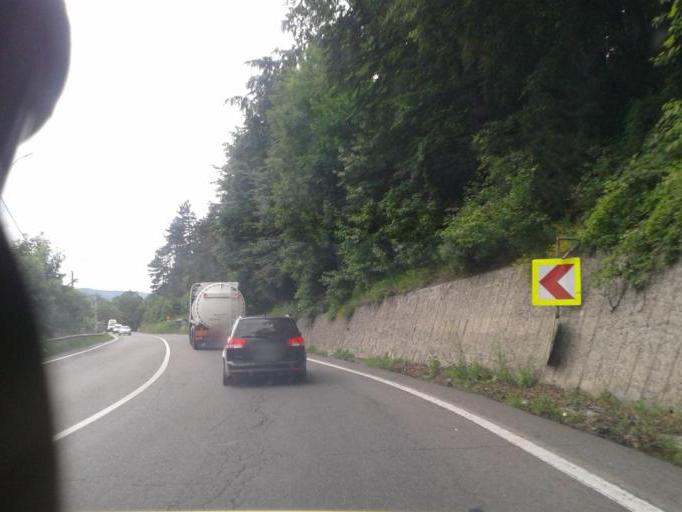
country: RO
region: Prahova
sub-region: Comuna Comarnic
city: Posada
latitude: 45.2899
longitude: 25.6138
